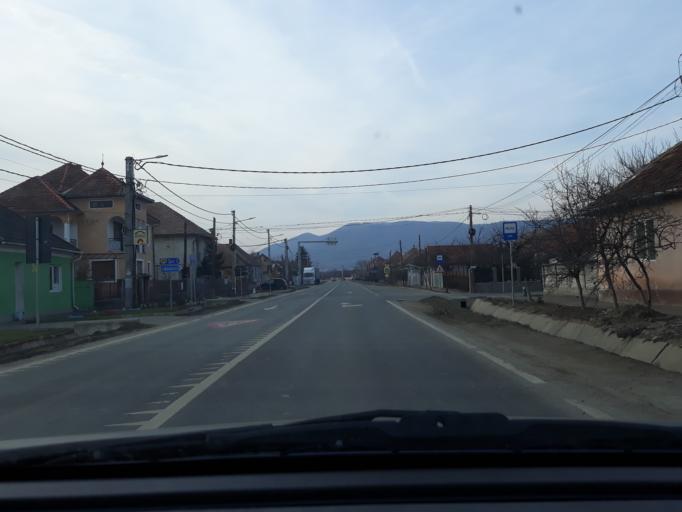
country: RO
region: Salaj
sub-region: Comuna Periceiu
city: Periceiu
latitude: 47.2261
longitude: 22.8614
